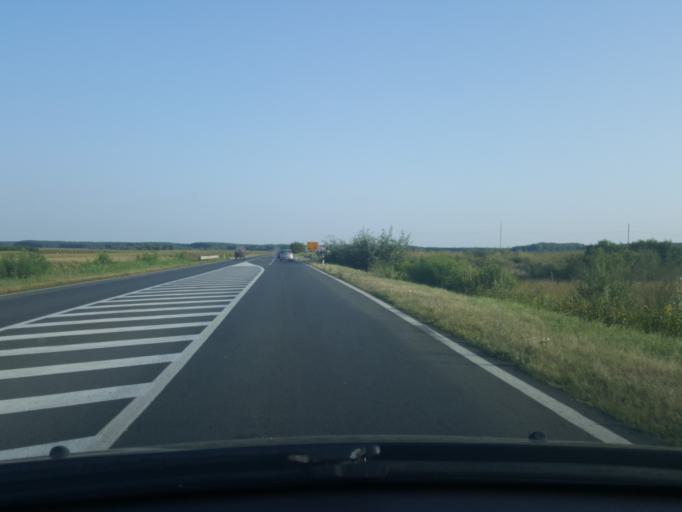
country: RS
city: Klenak
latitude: 44.7760
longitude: 19.7249
